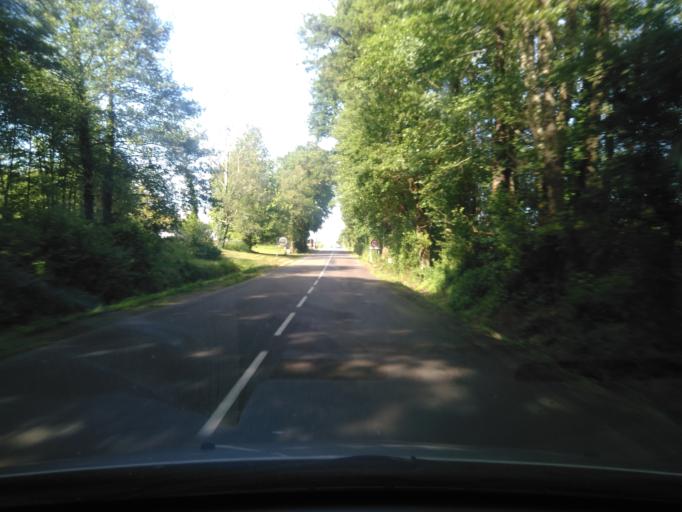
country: FR
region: Pays de la Loire
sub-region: Departement de la Vendee
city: Nieul-le-Dolent
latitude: 46.5434
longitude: -1.5337
